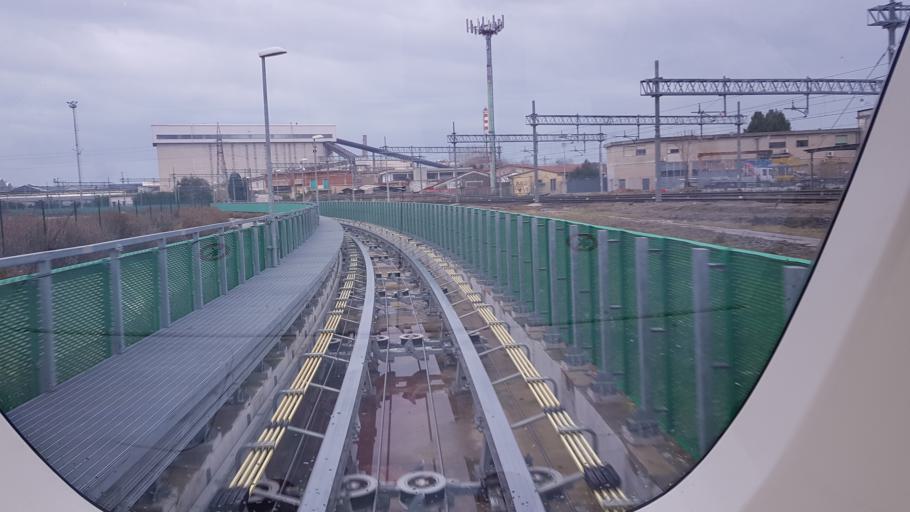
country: IT
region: Tuscany
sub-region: Province of Pisa
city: Pisa
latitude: 43.7081
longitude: 10.3944
